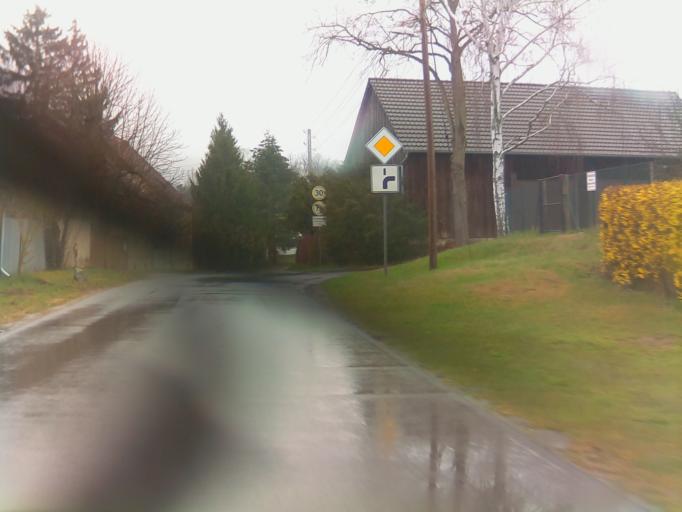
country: DE
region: Brandenburg
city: Jamlitz
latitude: 52.0179
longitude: 14.4082
